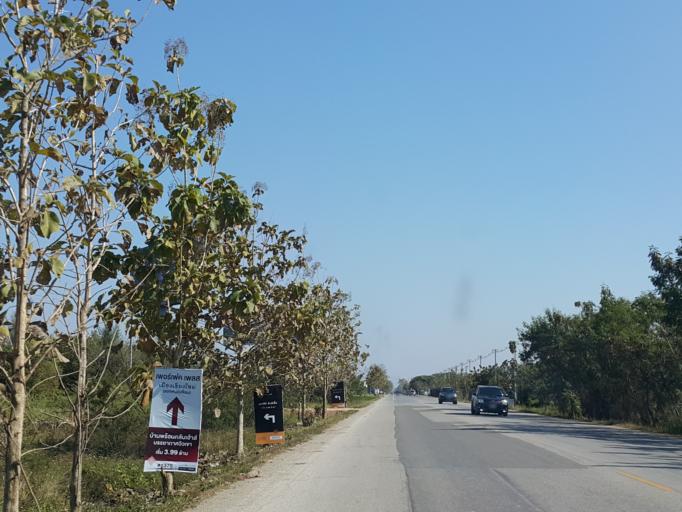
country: TH
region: Chiang Mai
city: San Sai
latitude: 18.8631
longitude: 98.9895
